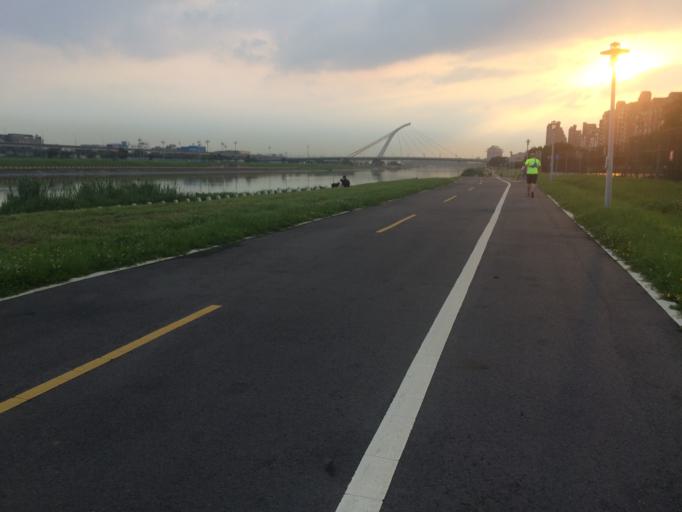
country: TW
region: Taipei
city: Taipei
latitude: 25.0765
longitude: 121.5536
